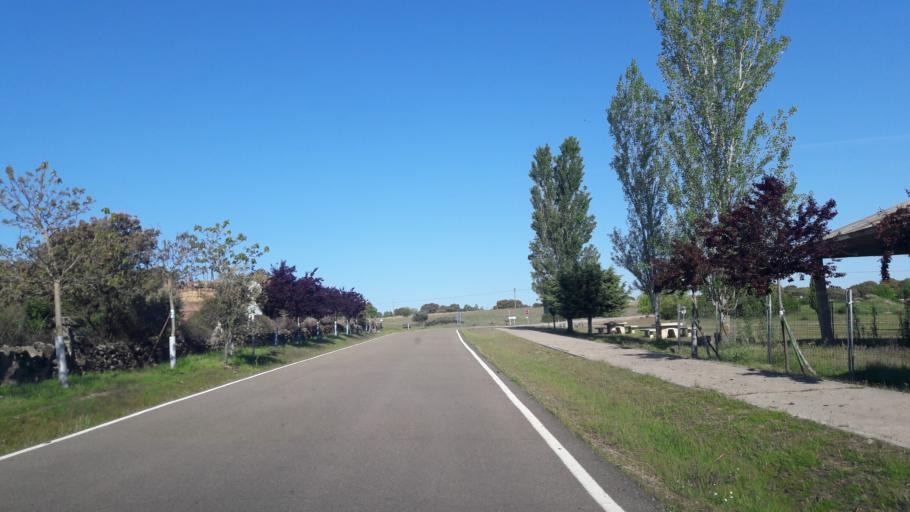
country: ES
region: Castille and Leon
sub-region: Provincia de Salamanca
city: Bogajo
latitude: 40.9071
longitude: -6.5359
